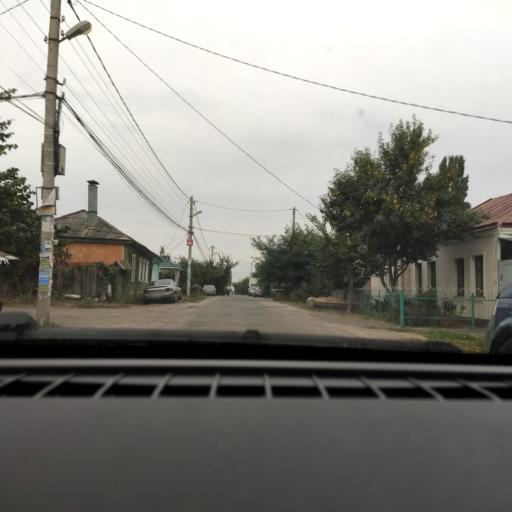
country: RU
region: Voronezj
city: Voronezh
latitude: 51.6717
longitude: 39.2643
